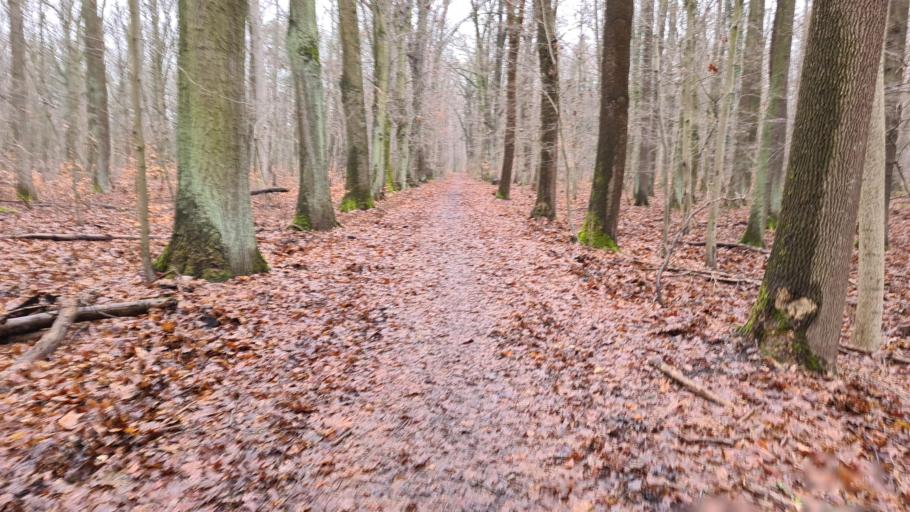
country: DE
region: Brandenburg
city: Finsterwalde
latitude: 51.6259
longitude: 13.6865
